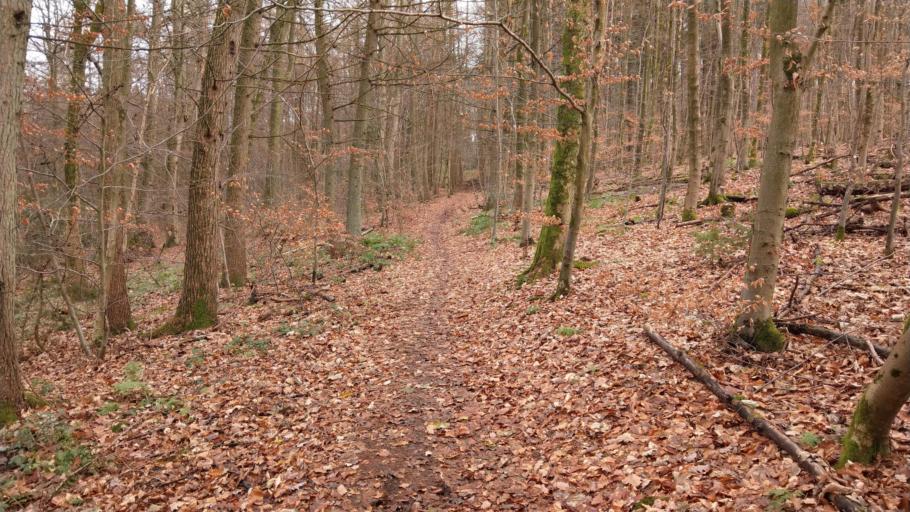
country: DE
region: North Rhine-Westphalia
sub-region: Regierungsbezirk Koln
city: Aachen
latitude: 50.7346
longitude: 6.0643
